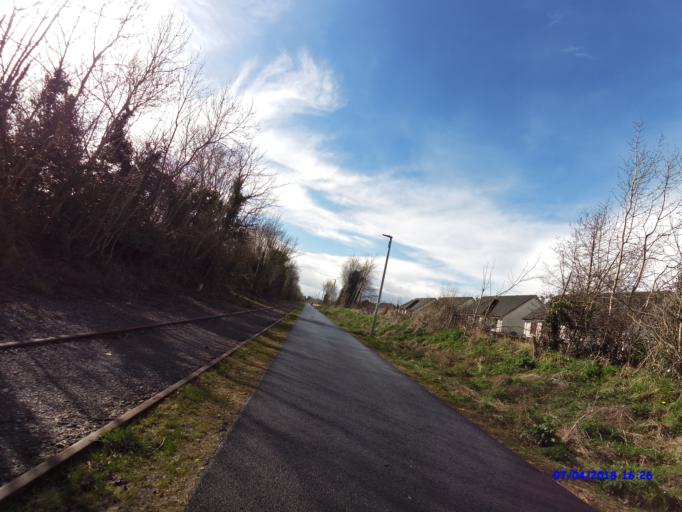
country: IE
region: Leinster
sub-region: An Iarmhi
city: Athlone
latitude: 53.4250
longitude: -7.9142
